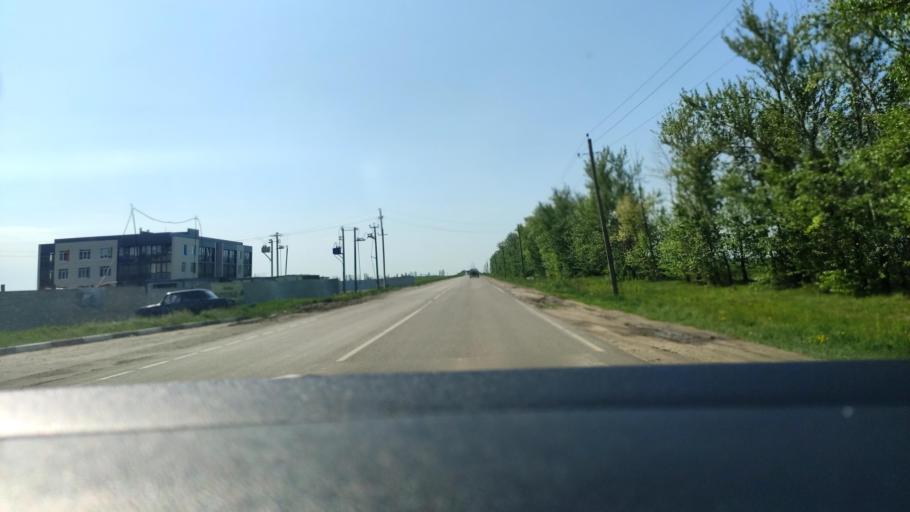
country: RU
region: Voronezj
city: Novaya Usman'
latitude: 51.6012
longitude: 39.3734
